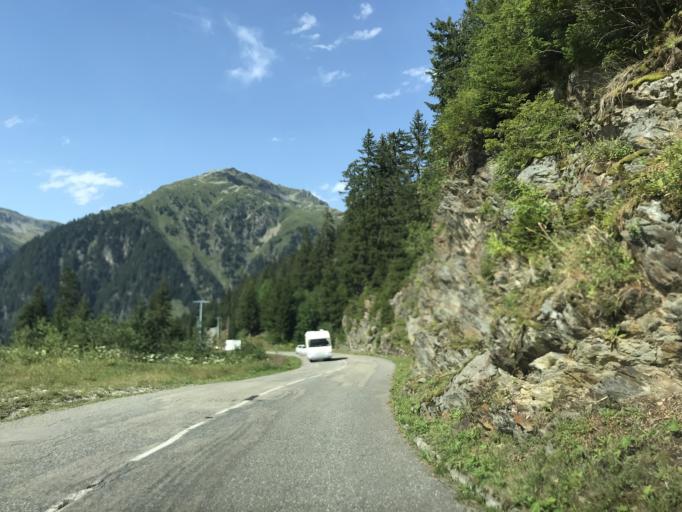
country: FR
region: Rhone-Alpes
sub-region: Departement de la Savoie
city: Beaufort
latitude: 45.6964
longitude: 6.6335
